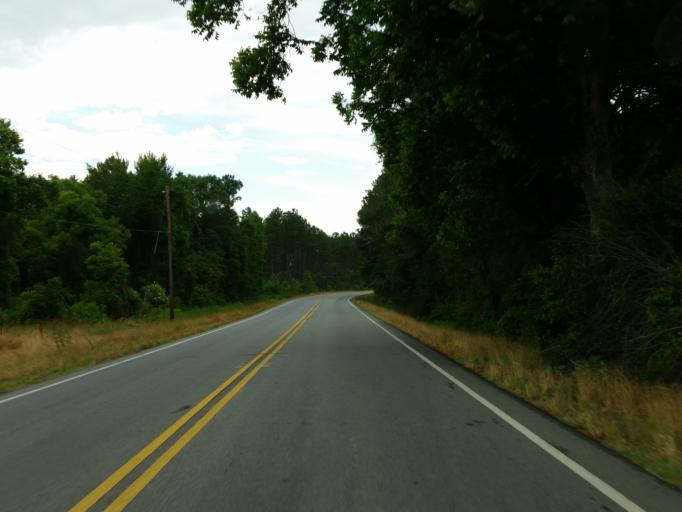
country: US
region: Georgia
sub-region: Dooly County
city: Vienna
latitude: 32.0652
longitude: -83.7985
